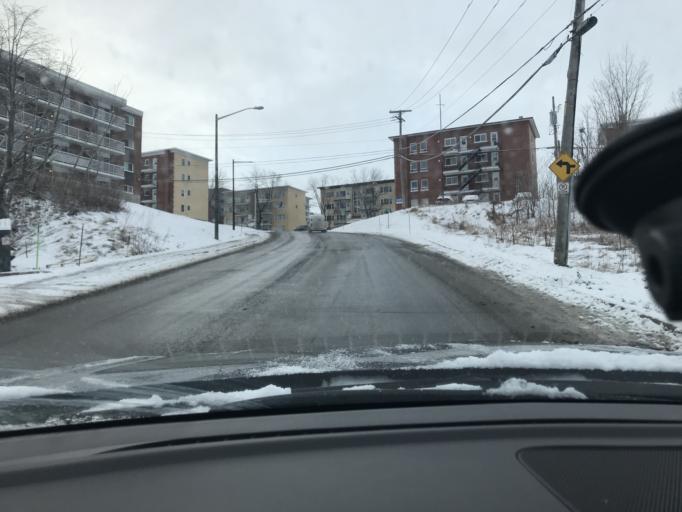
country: CA
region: Quebec
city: Quebec
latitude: 46.7926
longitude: -71.2734
